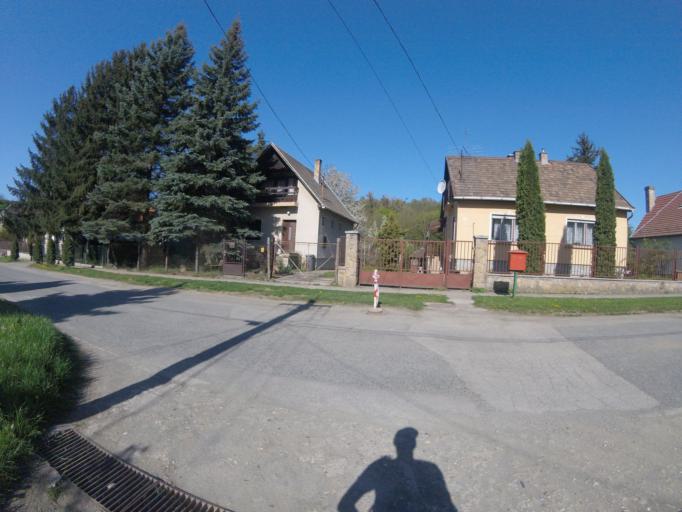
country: HU
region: Pest
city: Nagymaros
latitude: 47.8070
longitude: 18.9190
